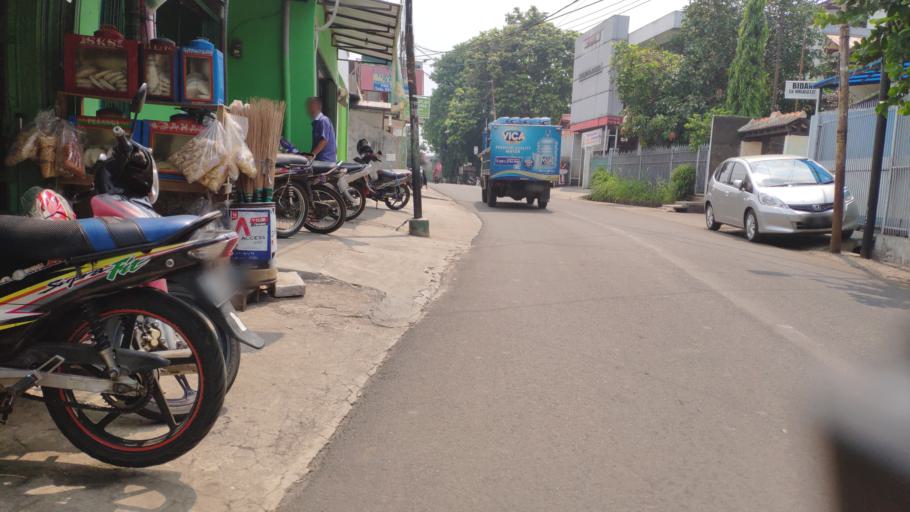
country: ID
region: West Java
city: Depok
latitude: -6.3266
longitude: 106.8246
